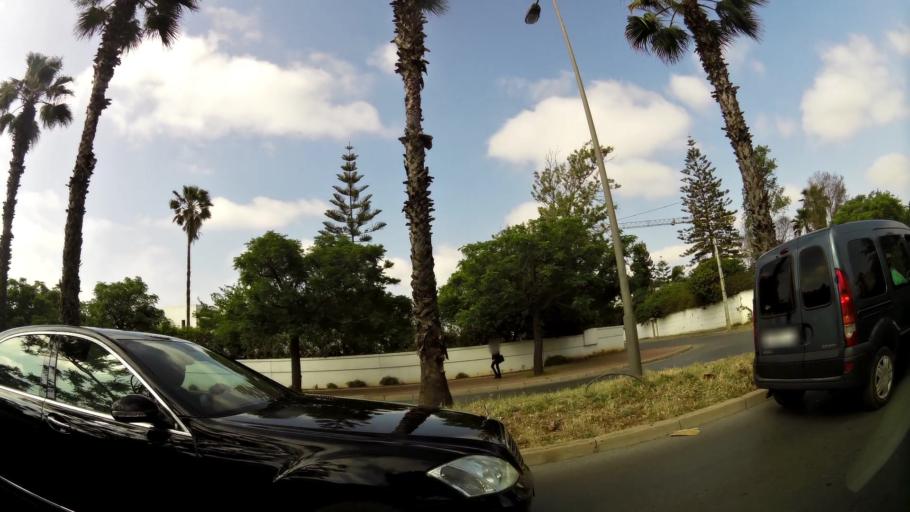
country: MA
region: Rabat-Sale-Zemmour-Zaer
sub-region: Rabat
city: Rabat
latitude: 33.9674
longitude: -6.8622
